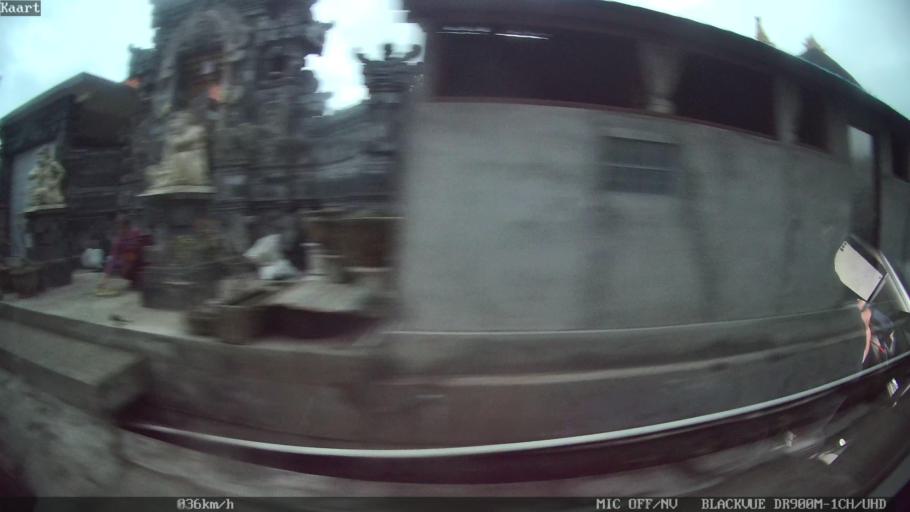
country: ID
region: Bali
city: Banjar Pasekan
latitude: -8.6130
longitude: 115.2864
